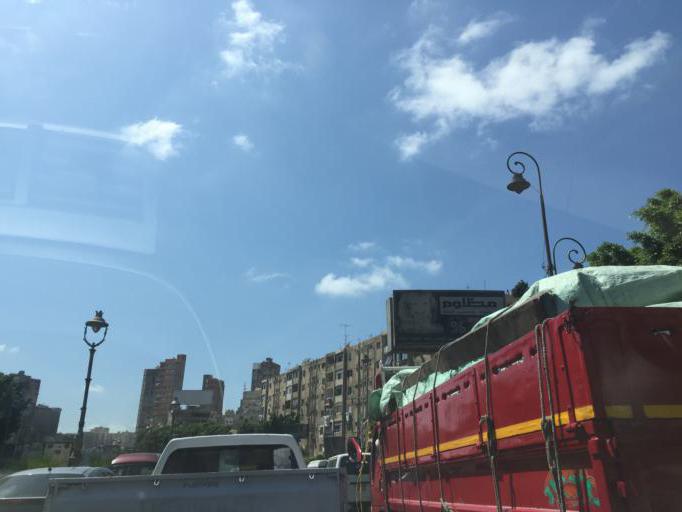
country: EG
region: Alexandria
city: Alexandria
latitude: 31.1946
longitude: 29.9220
